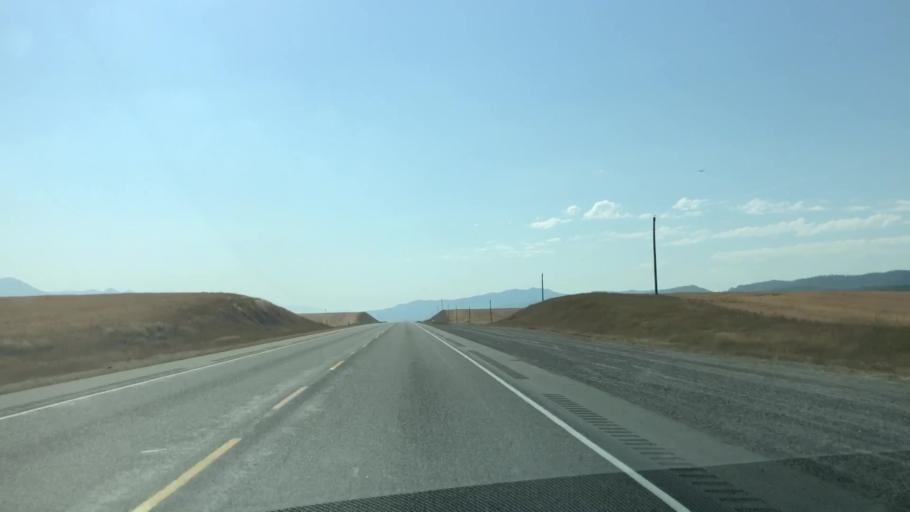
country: US
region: Idaho
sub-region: Teton County
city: Victor
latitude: 43.5141
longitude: -111.4830
